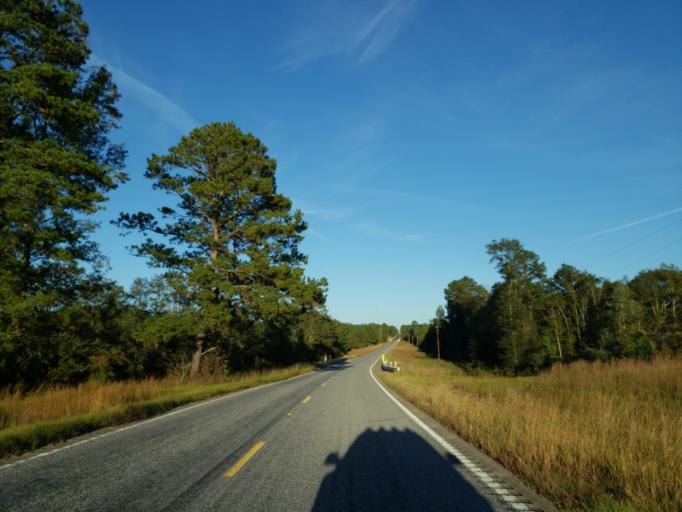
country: US
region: Mississippi
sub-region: Wayne County
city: Belmont
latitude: 31.4098
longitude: -88.6102
